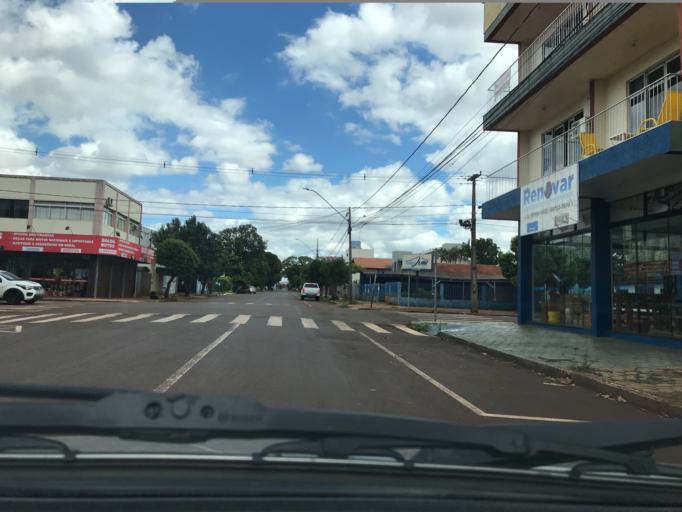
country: BR
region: Parana
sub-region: Palotina
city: Palotina
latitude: -24.2875
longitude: -53.8399
